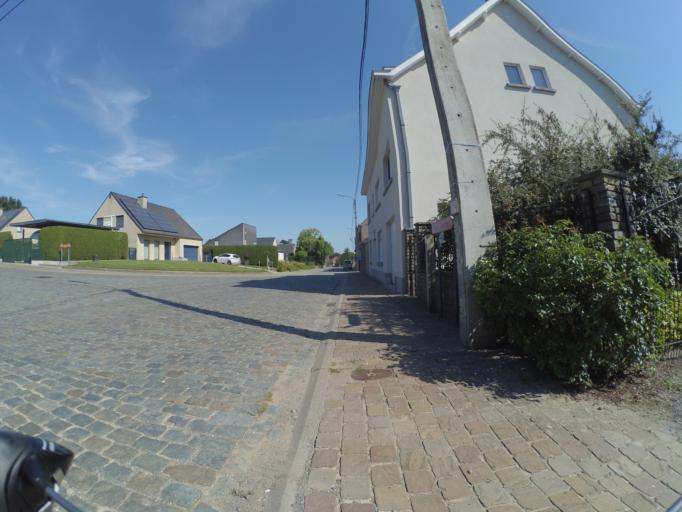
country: BE
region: Flanders
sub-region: Provincie Oost-Vlaanderen
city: Oudenaarde
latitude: 50.8005
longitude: 3.6214
